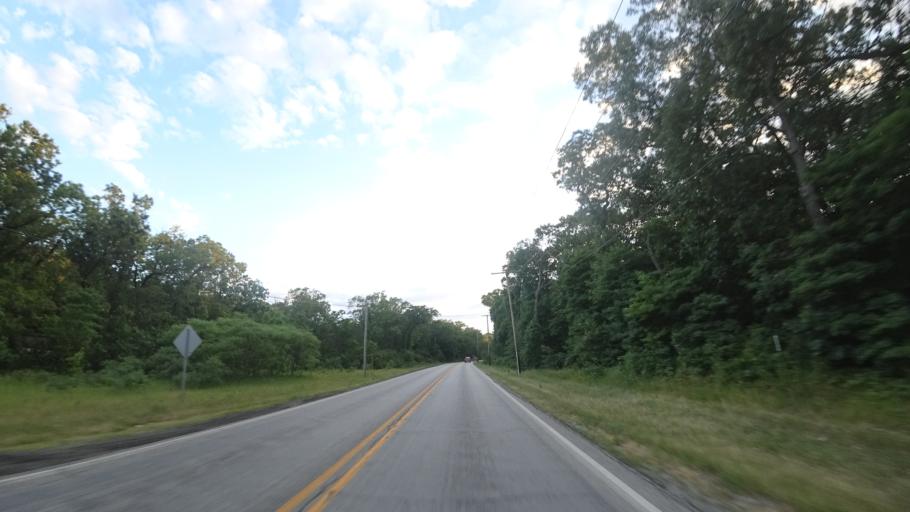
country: US
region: Indiana
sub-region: Porter County
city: Porter
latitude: 41.6398
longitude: -87.0695
